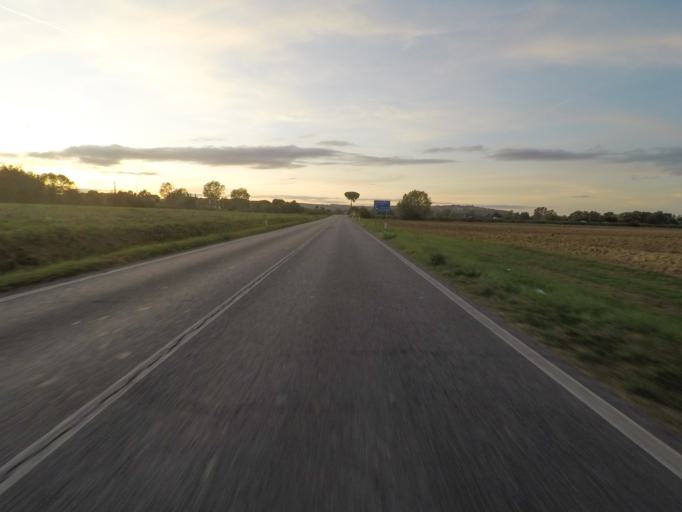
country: IT
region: Tuscany
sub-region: Provincia di Siena
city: Torrita di Siena
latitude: 43.1887
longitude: 11.7594
